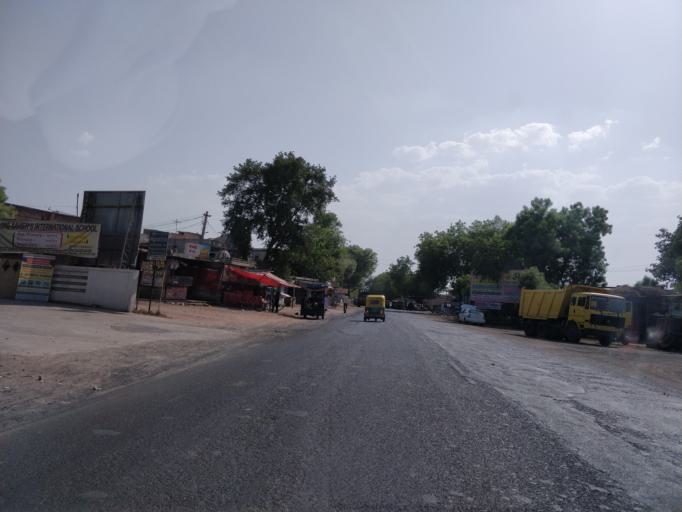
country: IN
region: Gujarat
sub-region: Ahmadabad
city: Naroda
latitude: 23.1008
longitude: 72.7057
